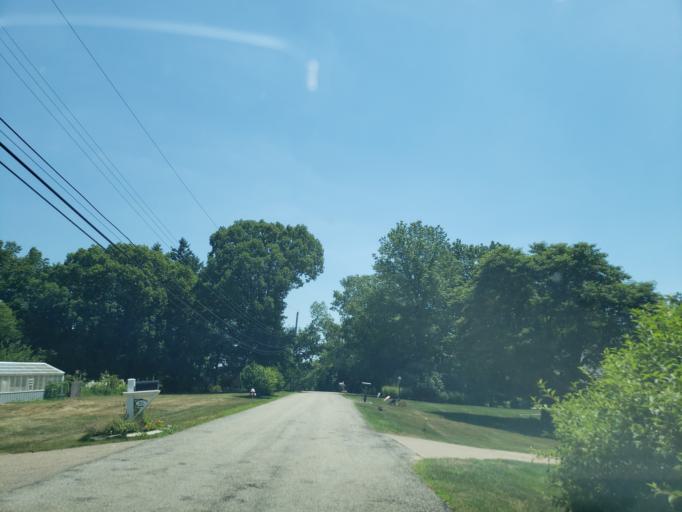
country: US
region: Pennsylvania
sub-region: Allegheny County
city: Emsworth
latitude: 40.5194
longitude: -80.0999
